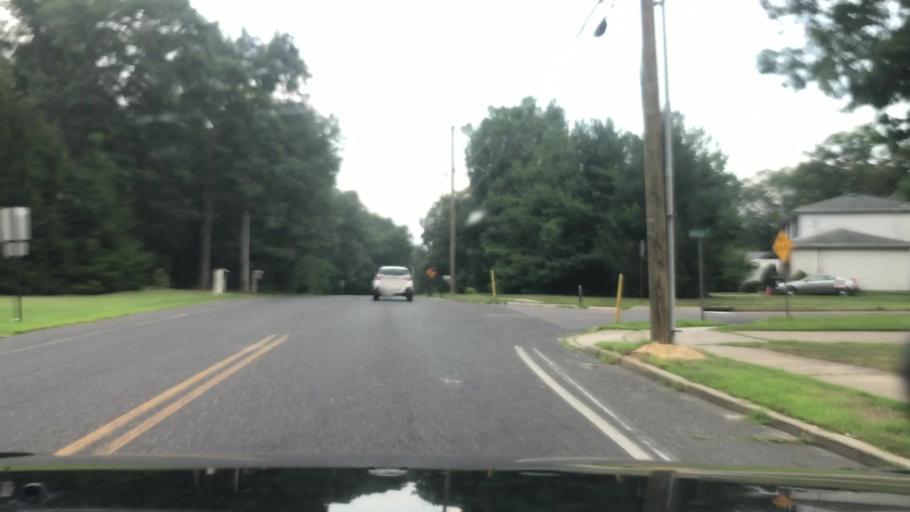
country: US
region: New Jersey
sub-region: Ocean County
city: Lakewood
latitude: 40.1058
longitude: -74.2741
